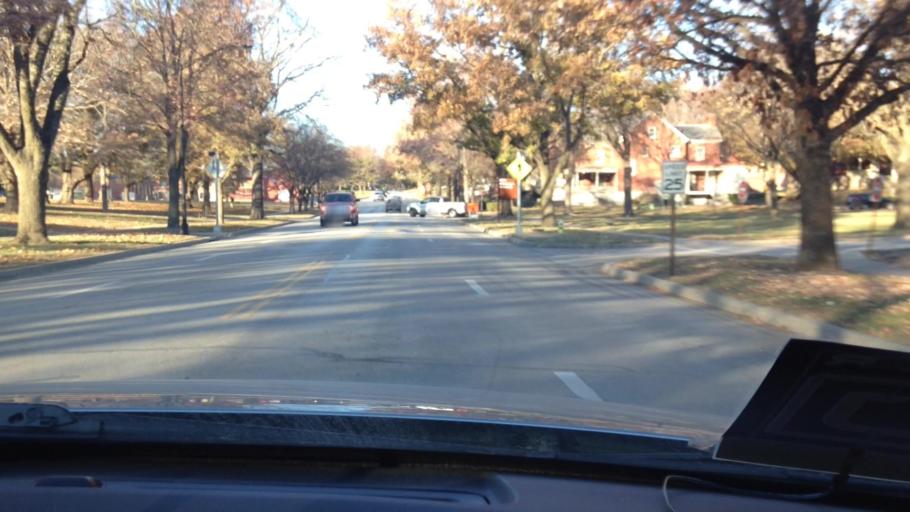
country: US
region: Kansas
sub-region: Leavenworth County
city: Leavenworth
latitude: 39.3498
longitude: -94.9188
